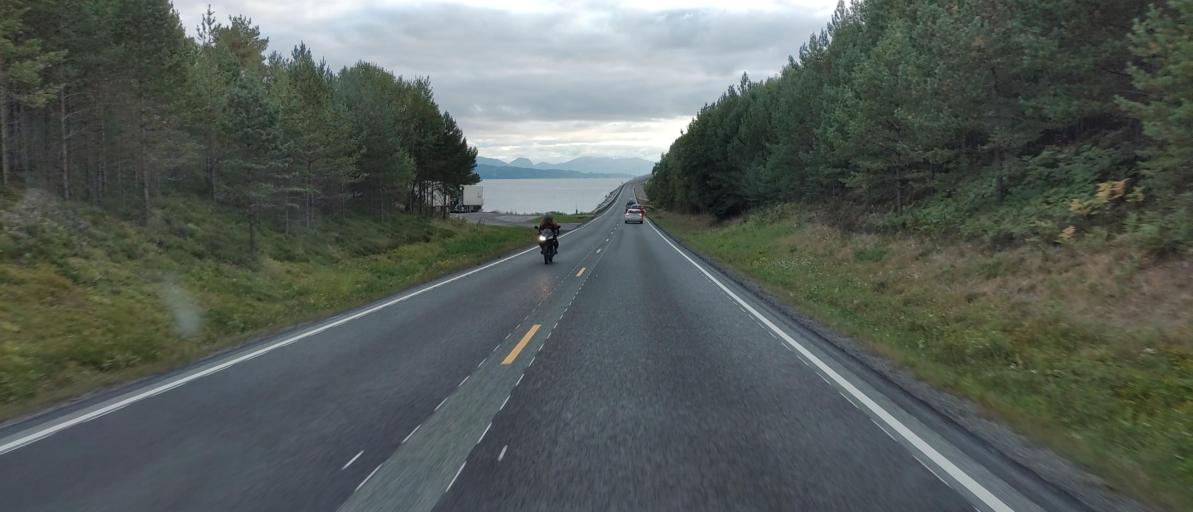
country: NO
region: More og Romsdal
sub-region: Molde
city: Hjelset
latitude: 62.7326
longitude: 7.3725
